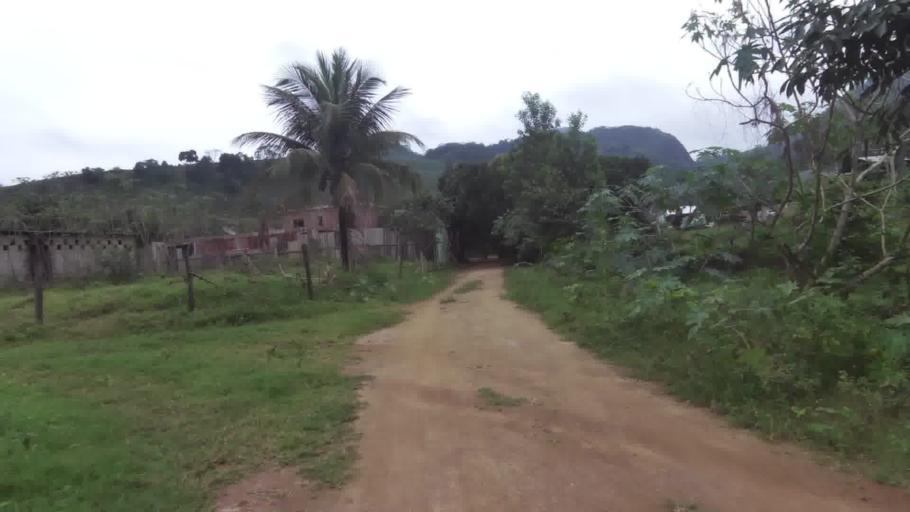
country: BR
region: Espirito Santo
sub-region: Iconha
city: Iconha
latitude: -20.7636
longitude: -40.8368
